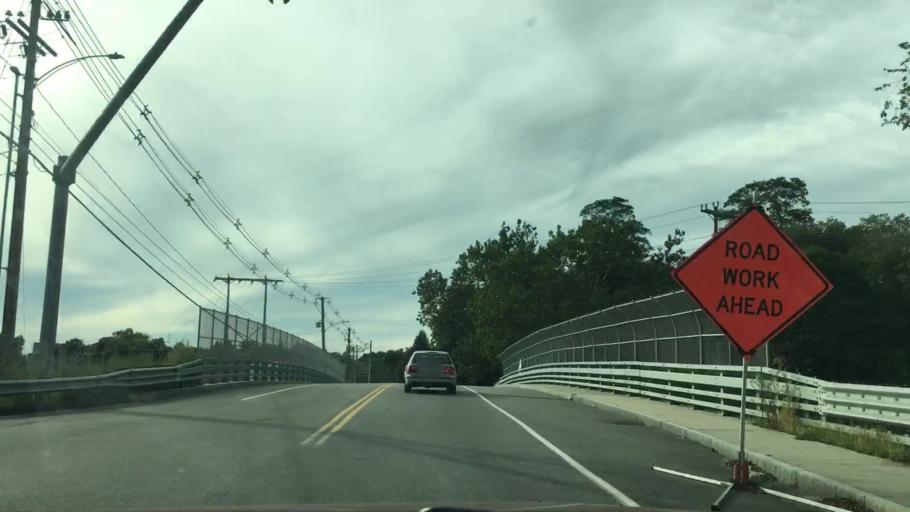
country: US
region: New Hampshire
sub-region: Rockingham County
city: Portsmouth
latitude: 43.0805
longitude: -70.7690
